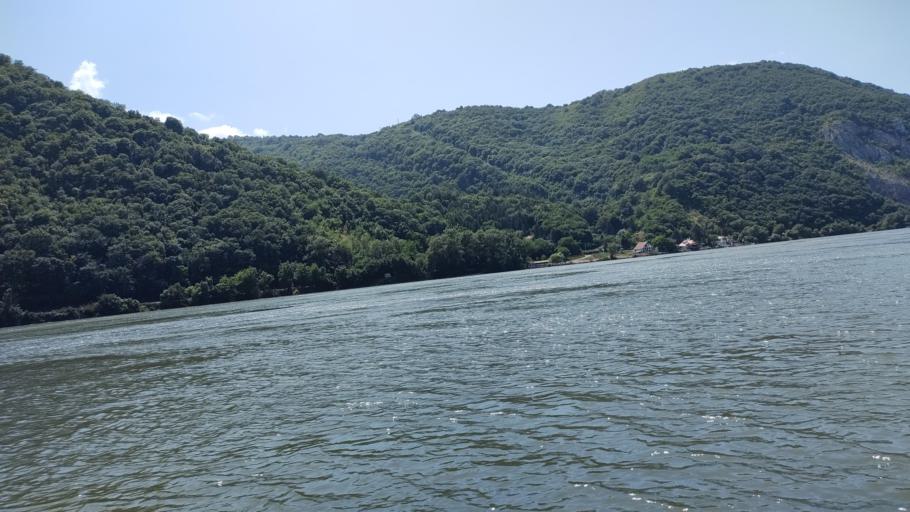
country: RO
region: Caras-Severin
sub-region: Comuna Pescari
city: Coronini
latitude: 44.6557
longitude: 21.7148
